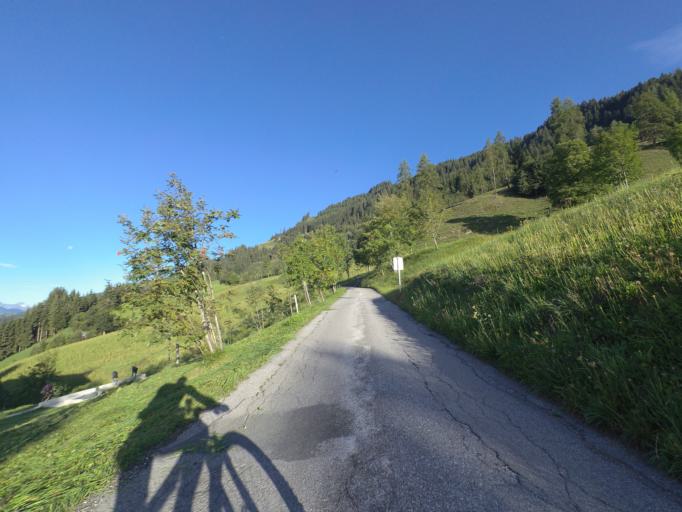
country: AT
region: Salzburg
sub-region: Politischer Bezirk Sankt Johann im Pongau
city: Goldegg
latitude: 47.3409
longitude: 13.1024
